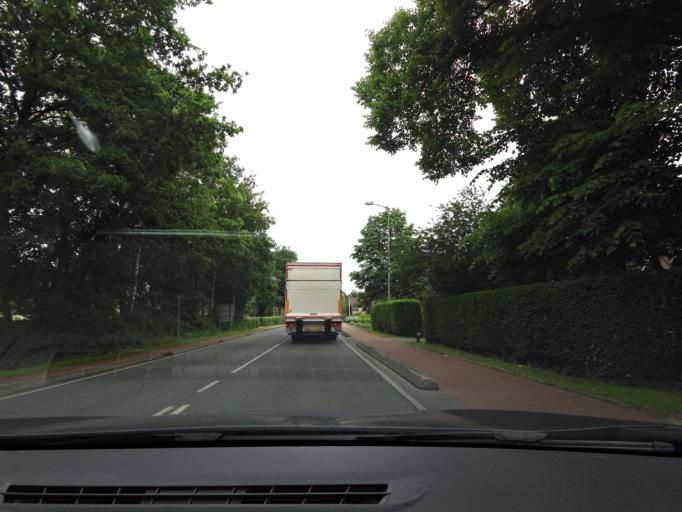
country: NL
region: Gelderland
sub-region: Gemeente Brummen
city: Eerbeek
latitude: 52.0978
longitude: 6.0516
